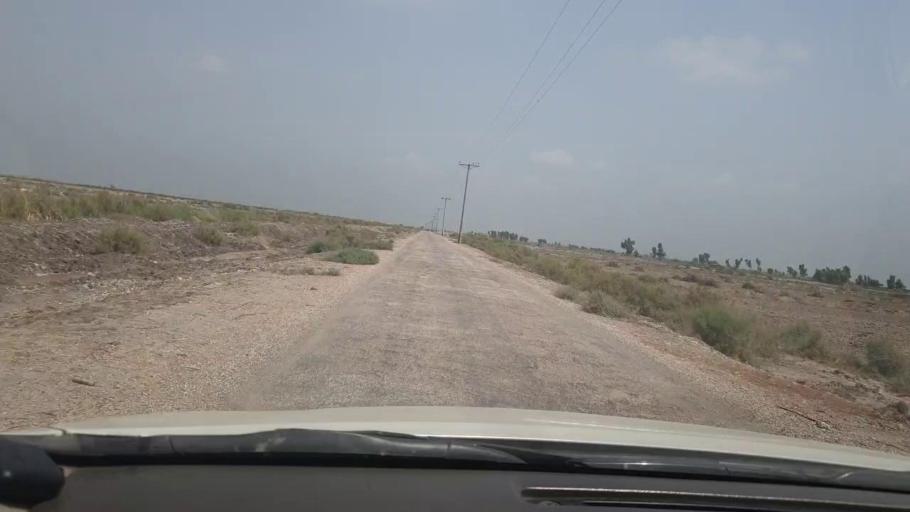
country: PK
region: Sindh
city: Garhi Yasin
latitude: 27.9930
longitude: 68.5012
